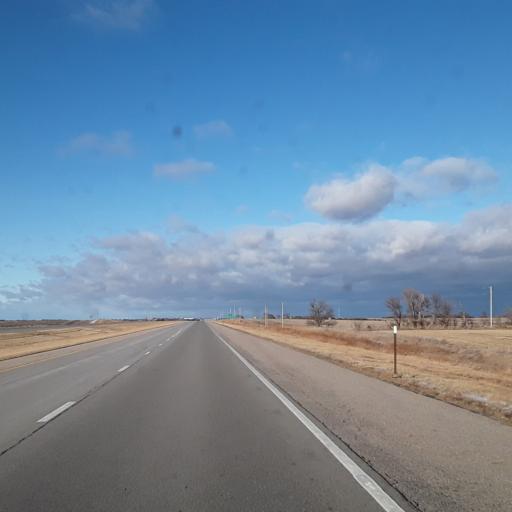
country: US
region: Kansas
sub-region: Republic County
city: Belleville
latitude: 39.9233
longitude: -97.6142
